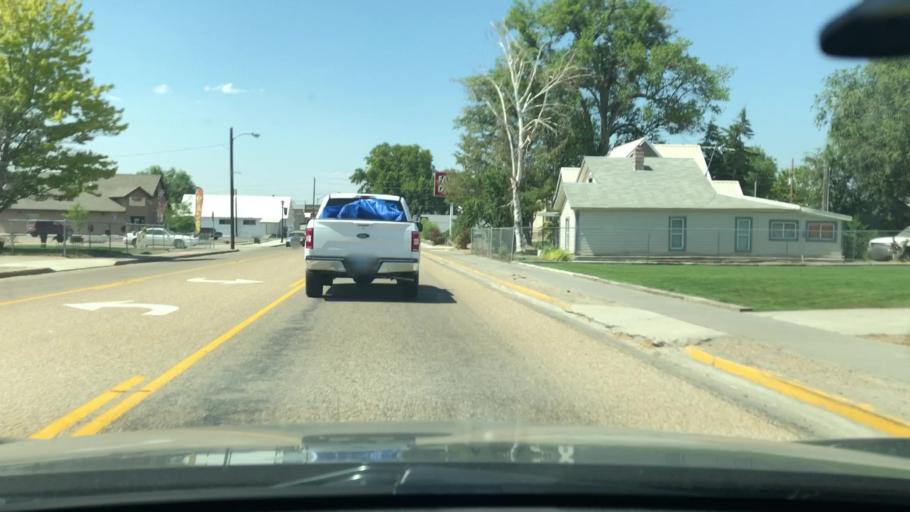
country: US
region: Idaho
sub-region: Canyon County
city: Parma
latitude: 43.7840
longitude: -116.9411
